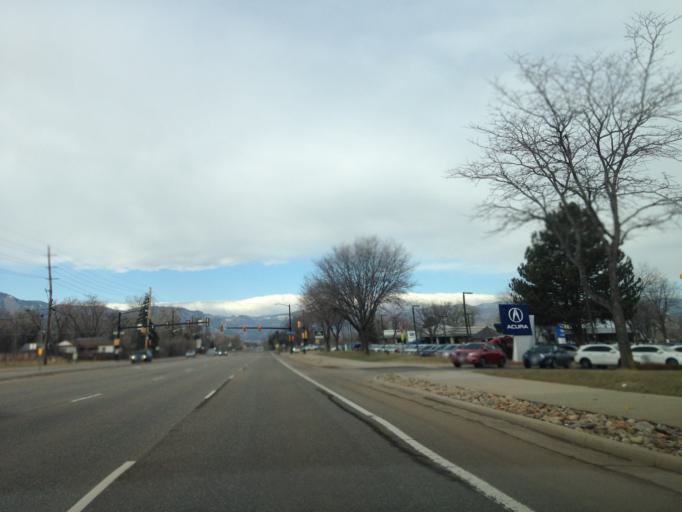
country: US
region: Colorado
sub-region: Boulder County
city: Boulder
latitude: 40.0149
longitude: -105.2111
